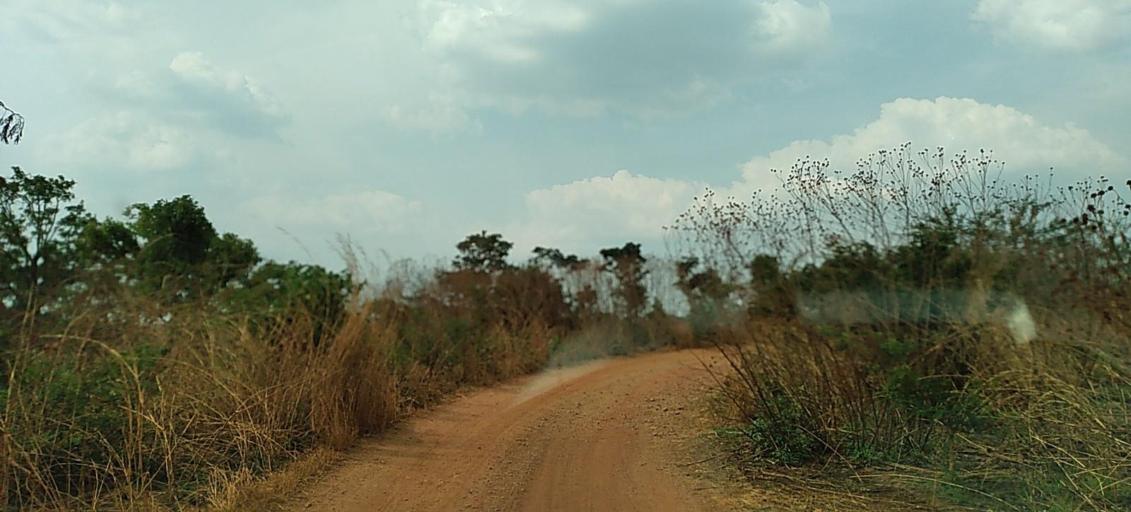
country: ZM
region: Copperbelt
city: Chililabombwe
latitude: -12.3942
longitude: 27.8037
